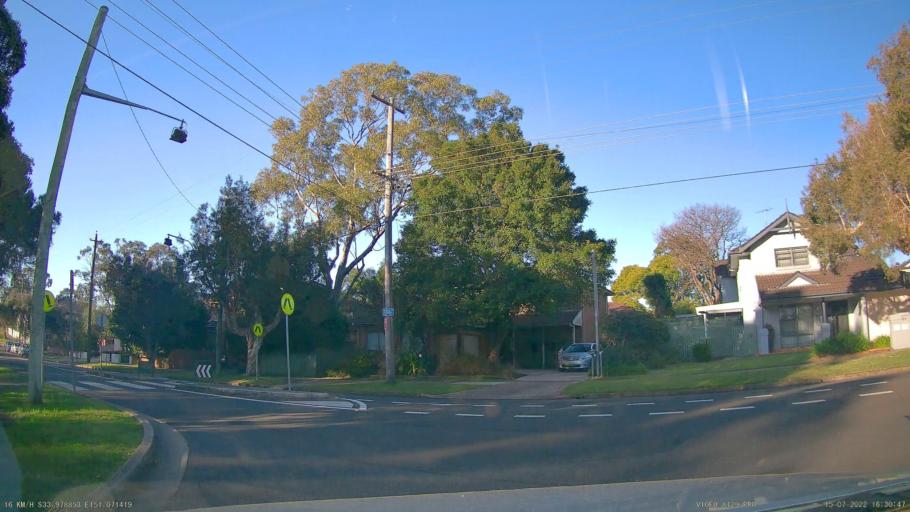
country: AU
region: New South Wales
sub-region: Hurstville
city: Oatley
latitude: -33.9788
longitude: 151.0715
